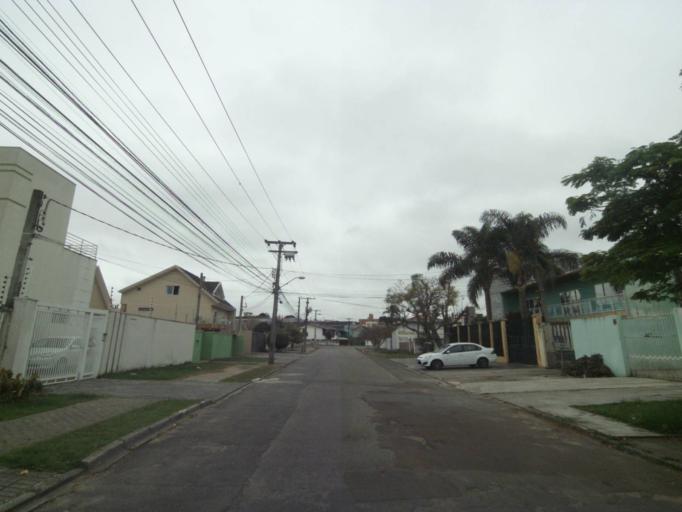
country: BR
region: Parana
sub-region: Curitiba
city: Curitiba
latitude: -25.4706
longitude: -49.2812
